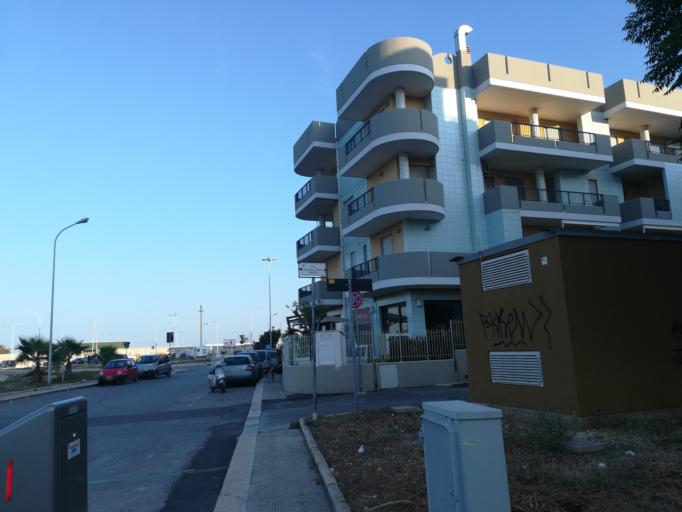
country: IT
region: Apulia
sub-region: Provincia di Bari
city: Polignano a Mare
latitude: 40.9934
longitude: 17.2289
